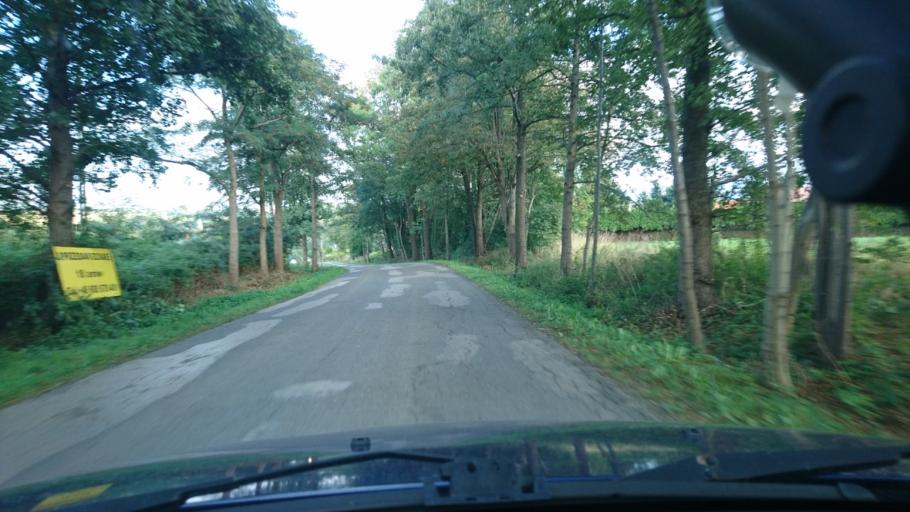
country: PL
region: Silesian Voivodeship
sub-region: Powiat bielski
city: Mazancowice
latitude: 49.8546
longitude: 18.9696
